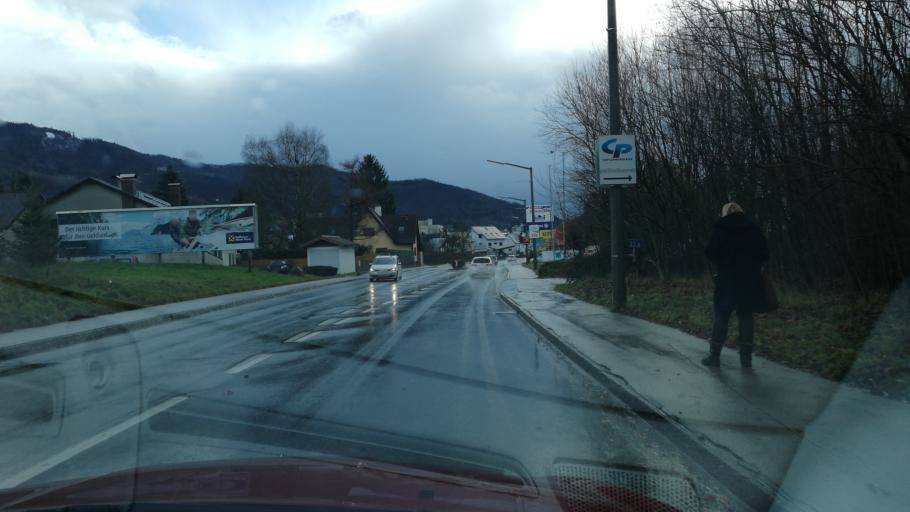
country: AT
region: Upper Austria
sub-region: Politischer Bezirk Kirchdorf an der Krems
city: Micheldorf in Oberoesterreich
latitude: 47.9014
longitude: 14.1254
